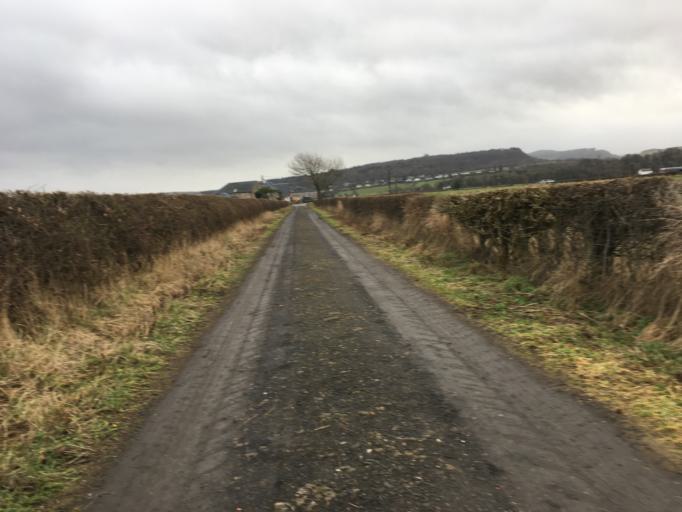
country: GB
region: Scotland
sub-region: Stirling
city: Stirling
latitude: 56.1247
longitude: -3.9762
